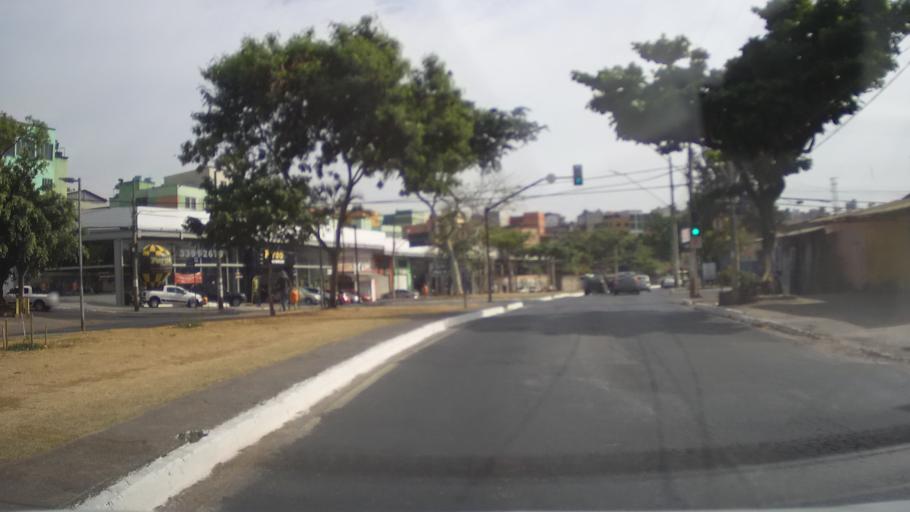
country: BR
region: Minas Gerais
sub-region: Contagem
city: Contagem
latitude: -19.9474
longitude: -44.0517
